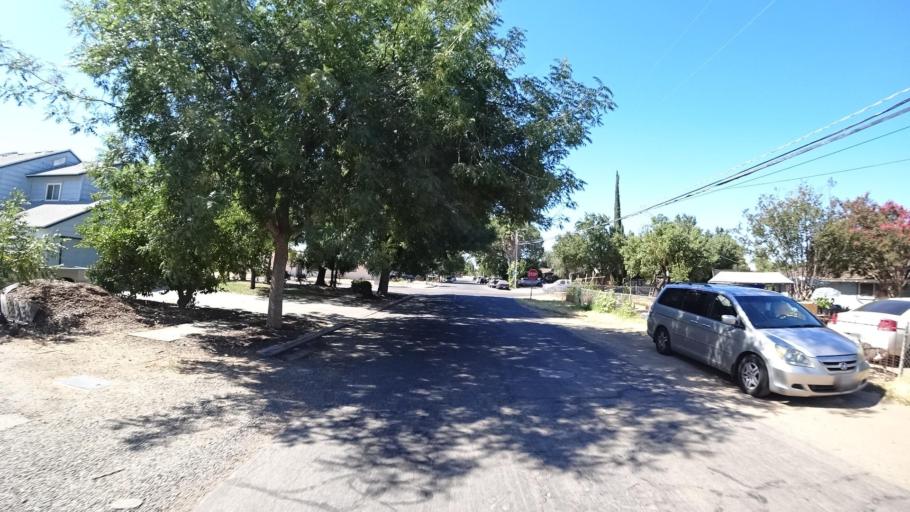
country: US
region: California
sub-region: Fresno County
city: Sunnyside
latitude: 36.7398
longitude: -119.7138
